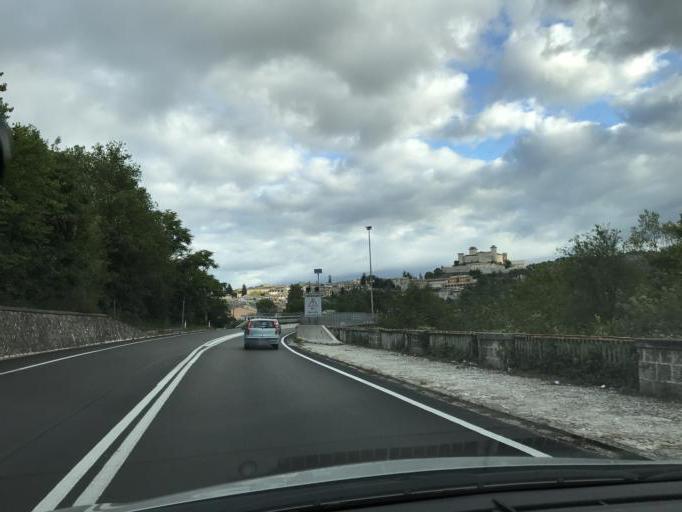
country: IT
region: Umbria
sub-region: Provincia di Perugia
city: Spoleto
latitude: 42.7260
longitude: 12.7348
